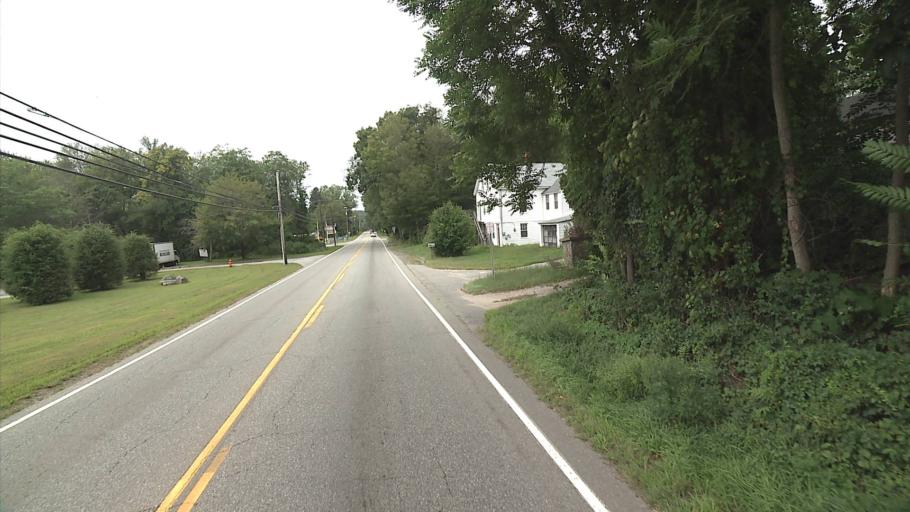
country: US
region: Connecticut
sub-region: New London County
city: Oxoboxo River
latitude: 41.3980
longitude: -72.1711
